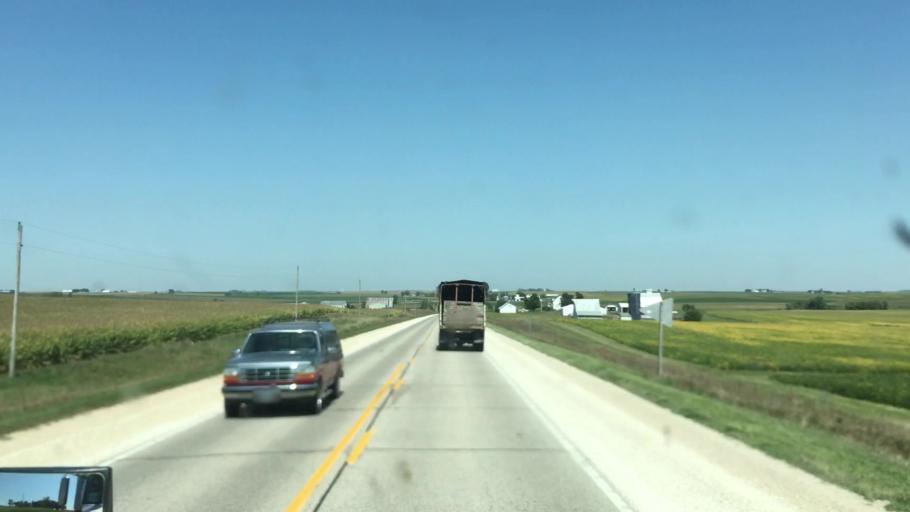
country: US
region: Iowa
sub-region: Tama County
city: Dysart
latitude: 42.0581
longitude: -92.2987
